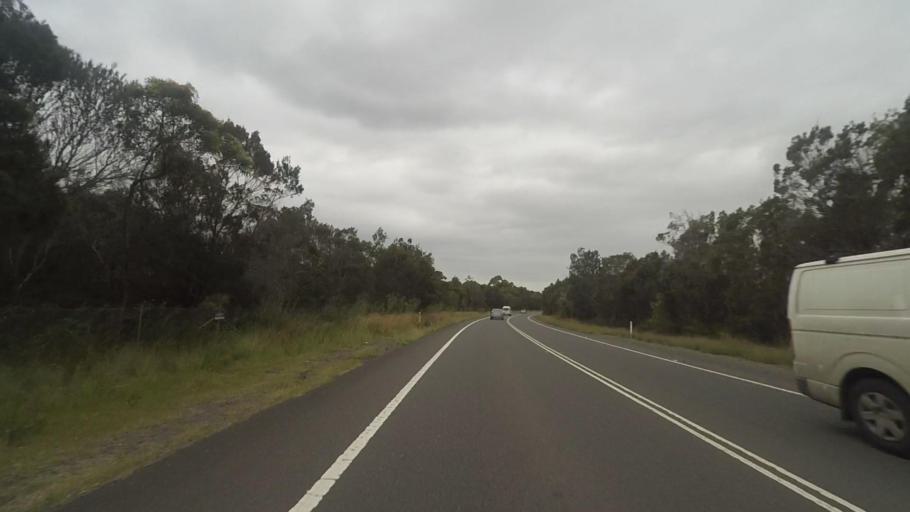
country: AU
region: New South Wales
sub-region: Sutherland Shire
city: Engadine
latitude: -34.0502
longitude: 150.9756
